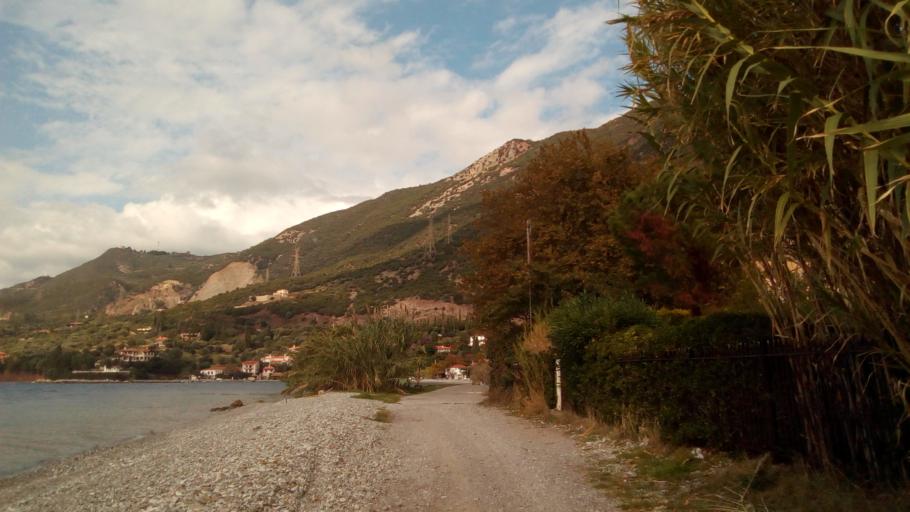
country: GR
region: West Greece
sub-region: Nomos Achaias
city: Kamarai
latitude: 38.3957
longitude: 21.9969
